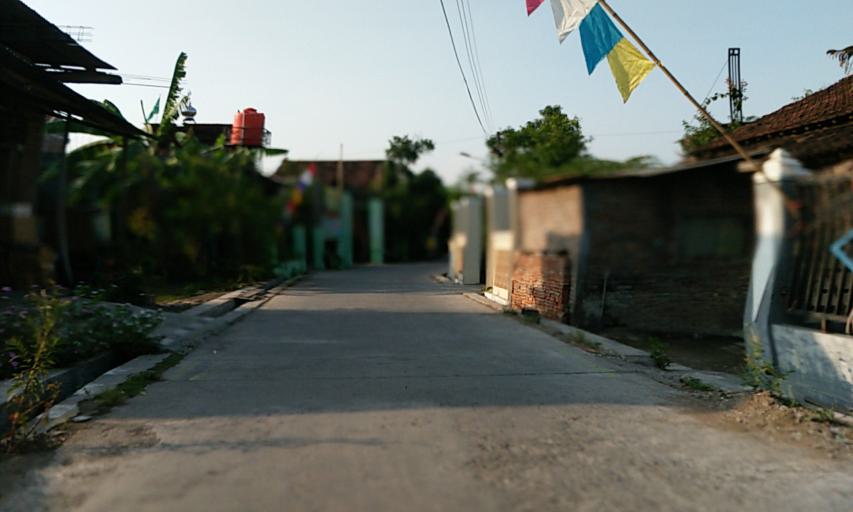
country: ID
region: Central Java
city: Mranggen
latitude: -7.0133
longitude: 110.4894
